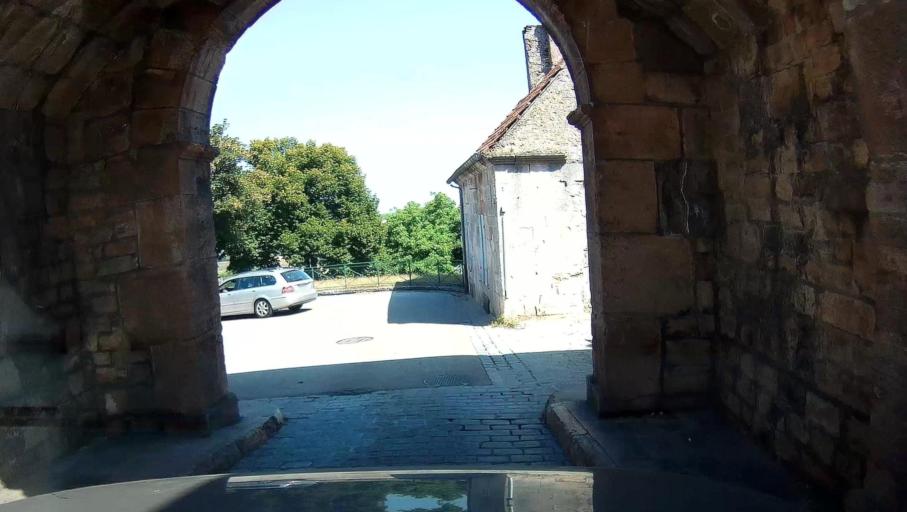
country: FR
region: Champagne-Ardenne
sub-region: Departement de la Haute-Marne
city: Langres
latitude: 47.8679
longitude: 5.3357
